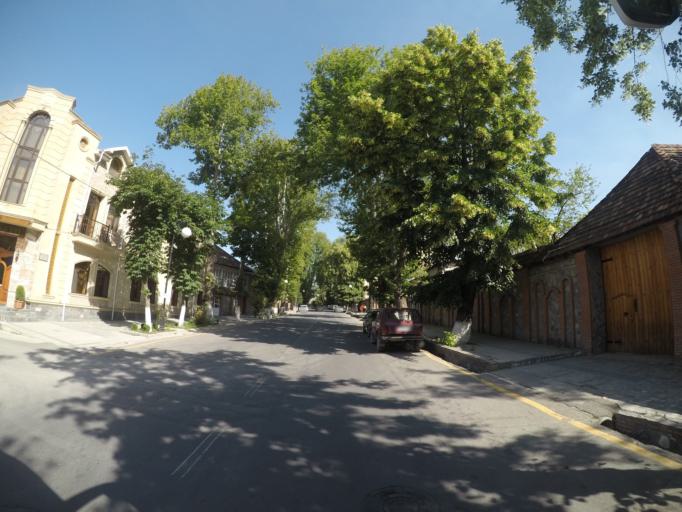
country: AZ
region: Shaki City
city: Sheki
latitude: 41.2043
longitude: 47.1783
